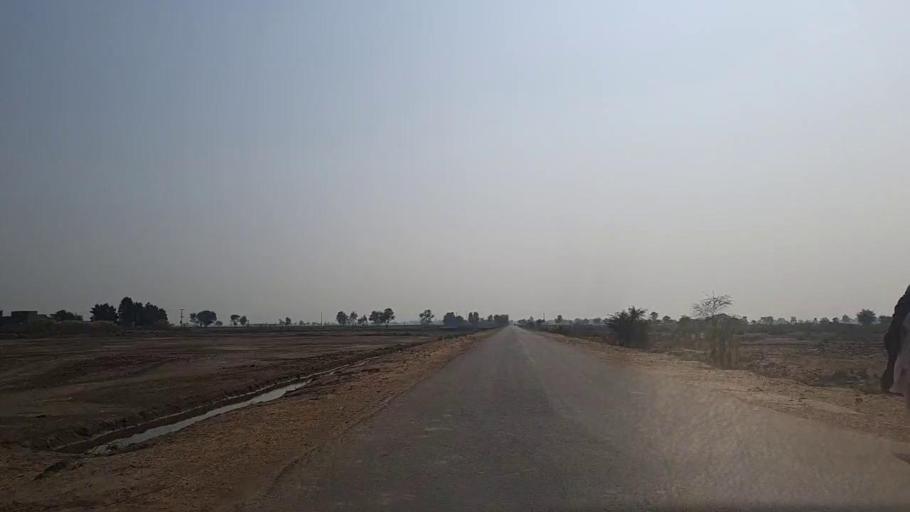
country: PK
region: Sindh
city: Jam Sahib
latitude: 26.3563
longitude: 68.5345
